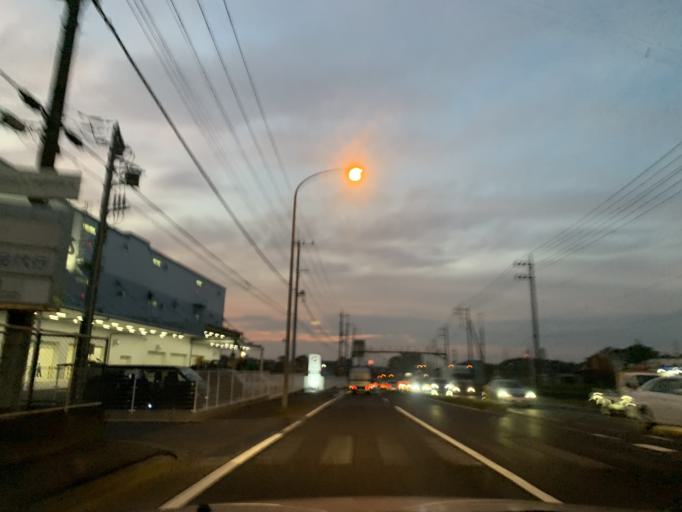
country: JP
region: Chiba
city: Nagareyama
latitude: 35.9122
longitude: 139.9321
